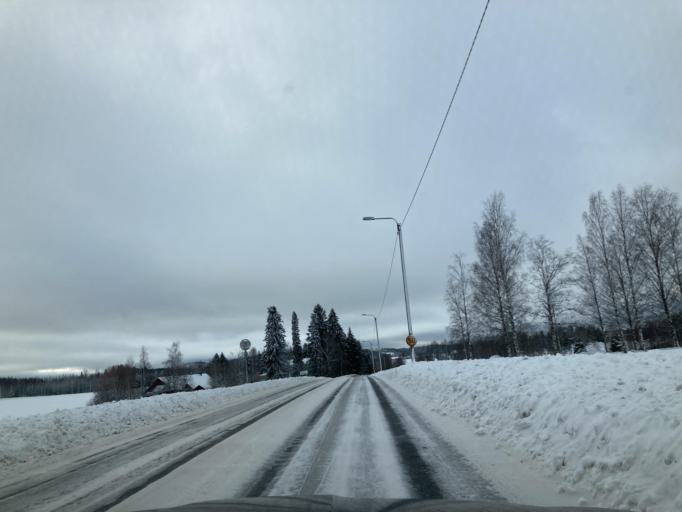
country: FI
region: Central Finland
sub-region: Jaemsae
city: Jaemsae
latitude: 61.8605
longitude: 25.2293
